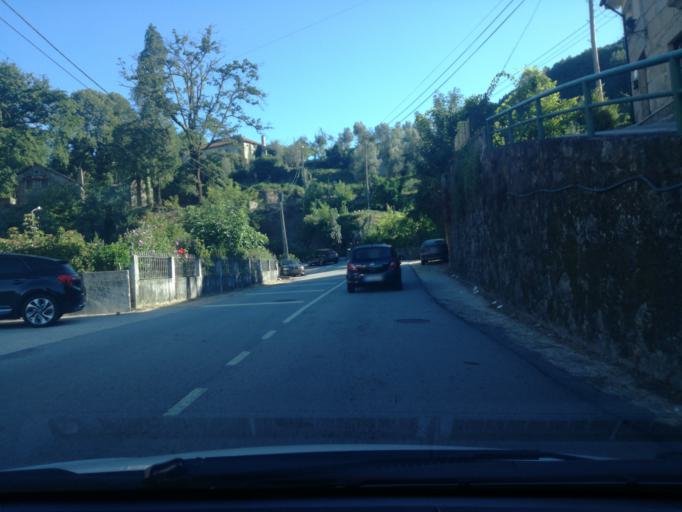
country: PT
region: Braga
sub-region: Vieira do Minho
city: Real
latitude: 41.7136
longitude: -8.1666
